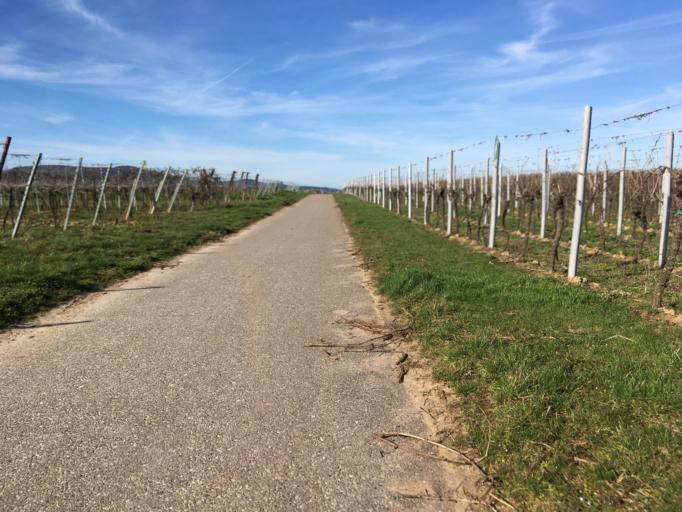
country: DE
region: Rheinland-Pfalz
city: Kirrweiler
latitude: 49.3161
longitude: 8.1522
